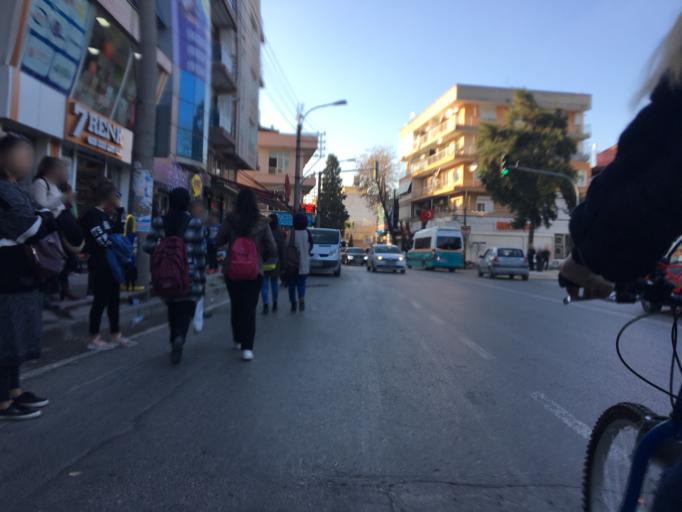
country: TR
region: Izmir
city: Buca
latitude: 38.3823
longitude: 27.1759
